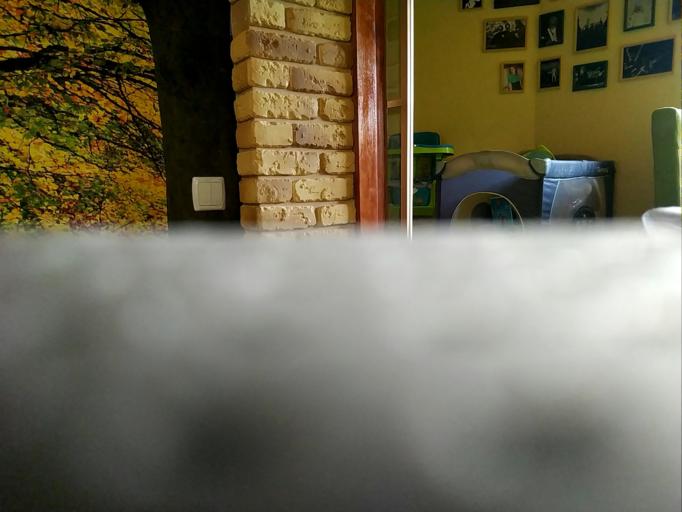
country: RU
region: Kaluga
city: Seredeyskiy
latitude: 54.0155
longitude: 35.3116
